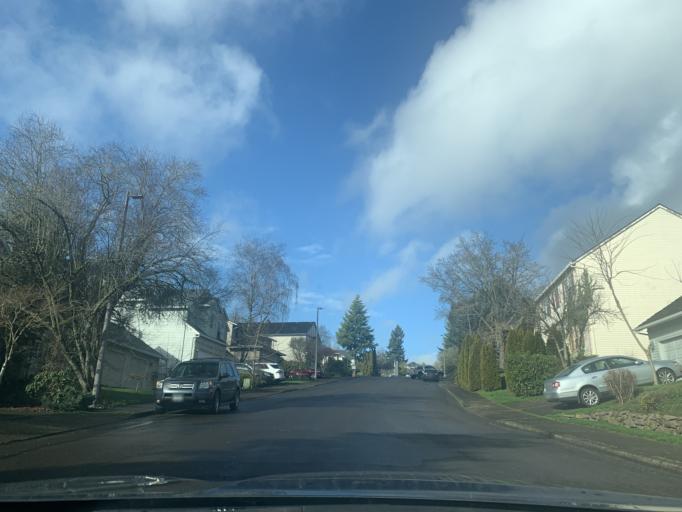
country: US
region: Oregon
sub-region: Washington County
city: King City
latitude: 45.4040
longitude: -122.8229
